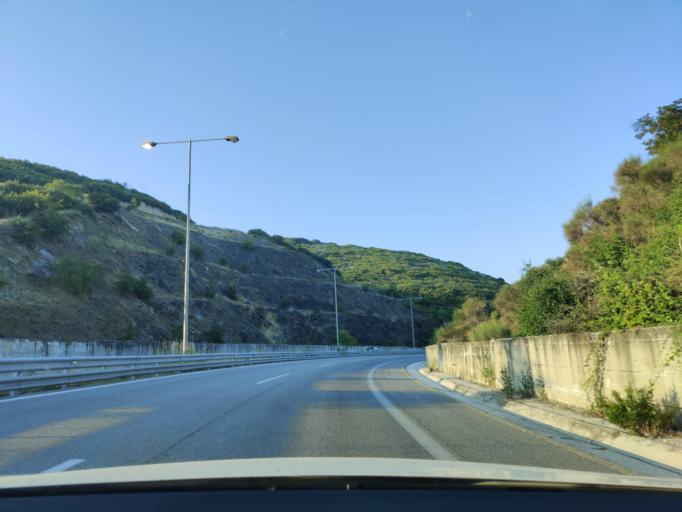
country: GR
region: East Macedonia and Thrace
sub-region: Nomos Kavalas
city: Kavala
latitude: 40.9602
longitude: 24.3920
